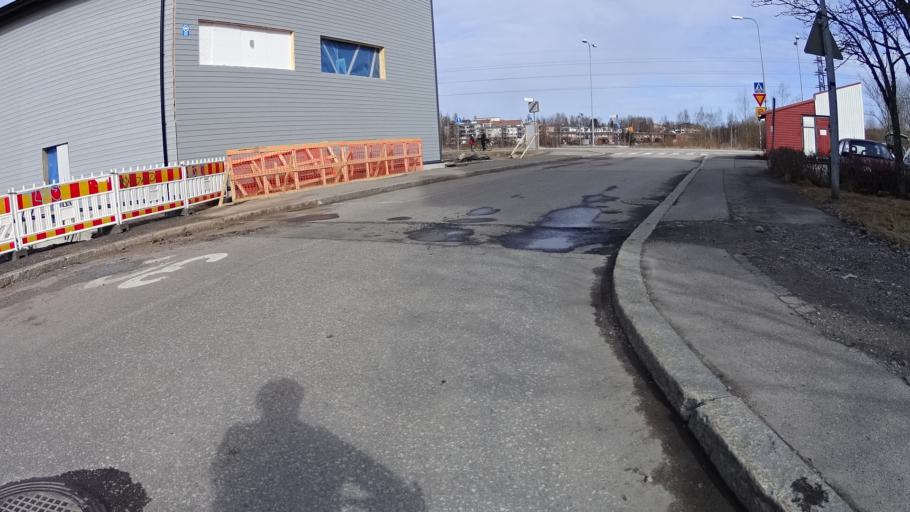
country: FI
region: Uusimaa
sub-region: Helsinki
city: Teekkarikylae
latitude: 60.2532
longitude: 24.8589
